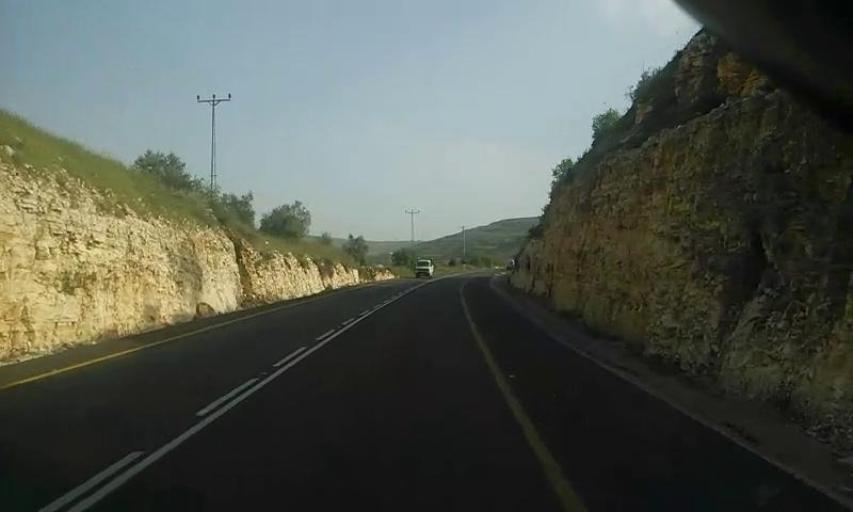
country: PS
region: West Bank
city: Jit
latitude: 32.2204
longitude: 35.1743
